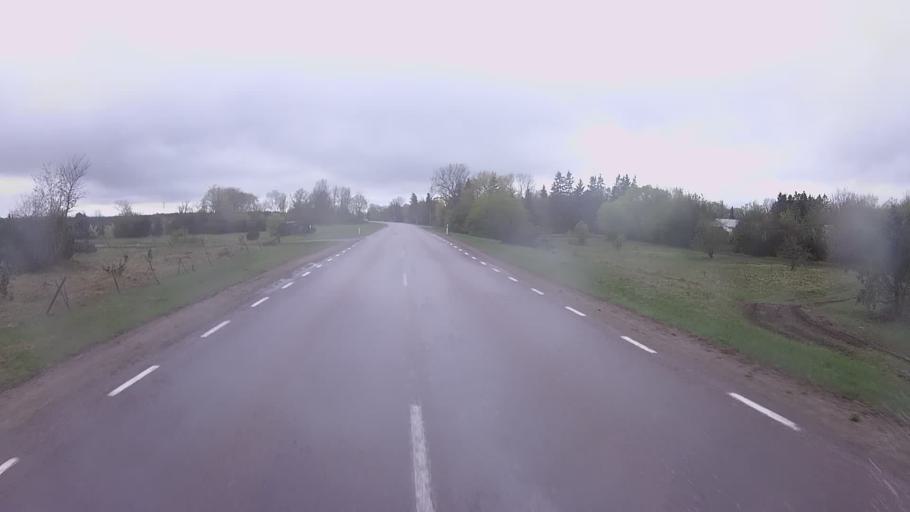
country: EE
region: Saare
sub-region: Kuressaare linn
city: Kuressaare
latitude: 58.3308
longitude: 22.5611
